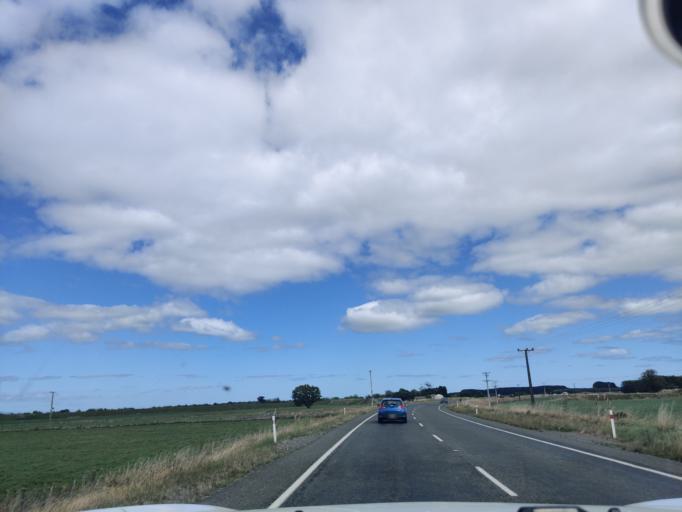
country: NZ
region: Manawatu-Wanganui
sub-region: Horowhenua District
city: Foxton
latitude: -40.4250
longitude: 175.4596
